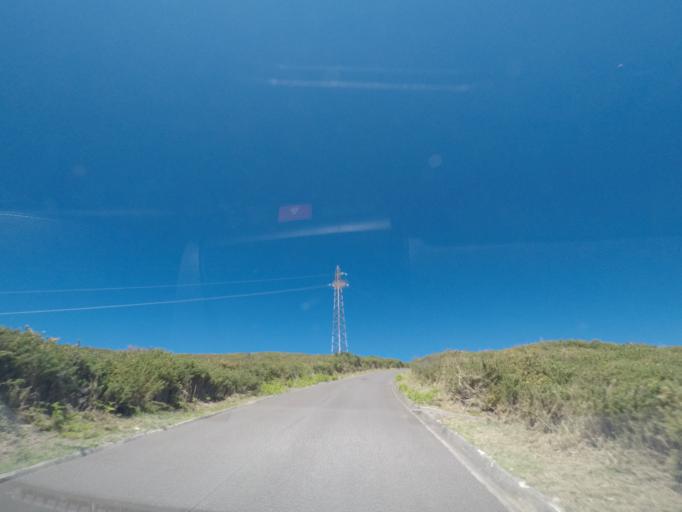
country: PT
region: Madeira
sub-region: Calheta
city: Arco da Calheta
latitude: 32.7474
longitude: -17.1265
